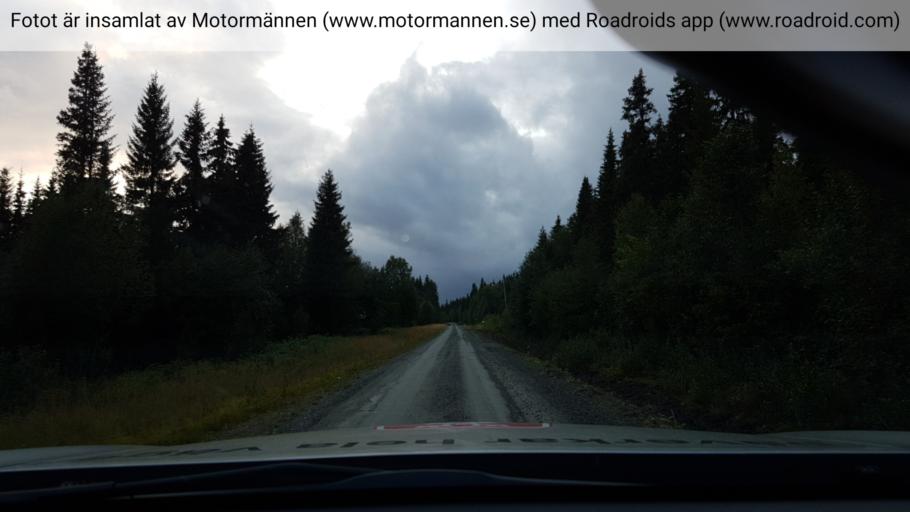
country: SE
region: Vaesterbotten
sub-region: Vilhelmina Kommun
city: Sjoberg
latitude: 65.4992
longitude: 15.5801
